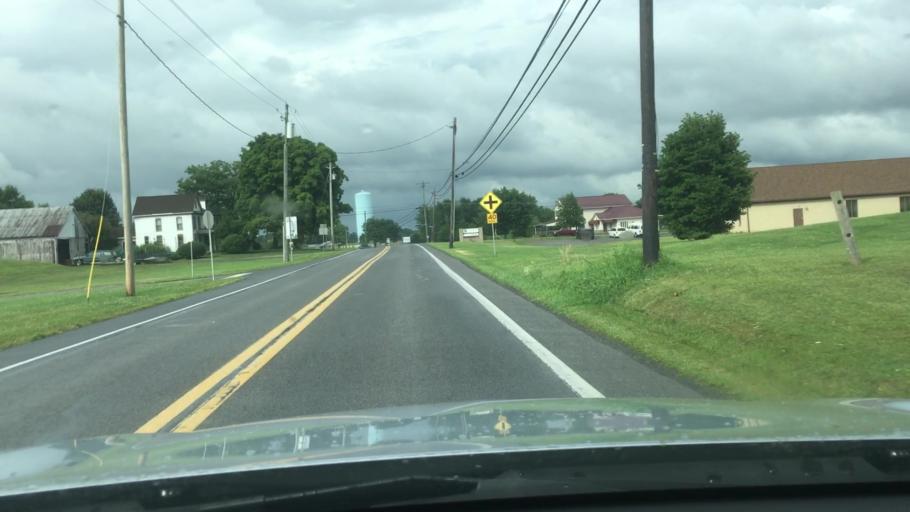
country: US
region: Pennsylvania
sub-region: Franklin County
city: Chambersburg
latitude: 39.9104
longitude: -77.7084
